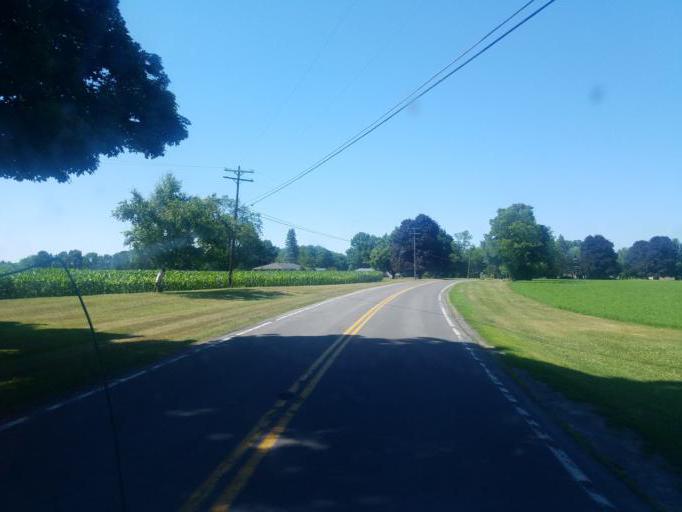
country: US
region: New York
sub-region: Ontario County
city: Geneva
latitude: 42.9256
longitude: -76.9989
